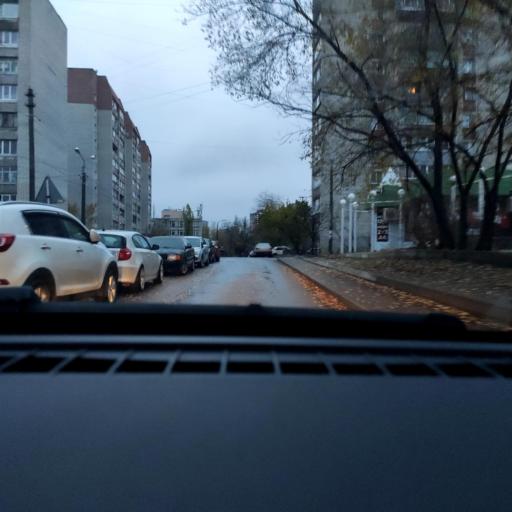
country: RU
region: Voronezj
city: Voronezh
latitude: 51.7123
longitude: 39.2712
